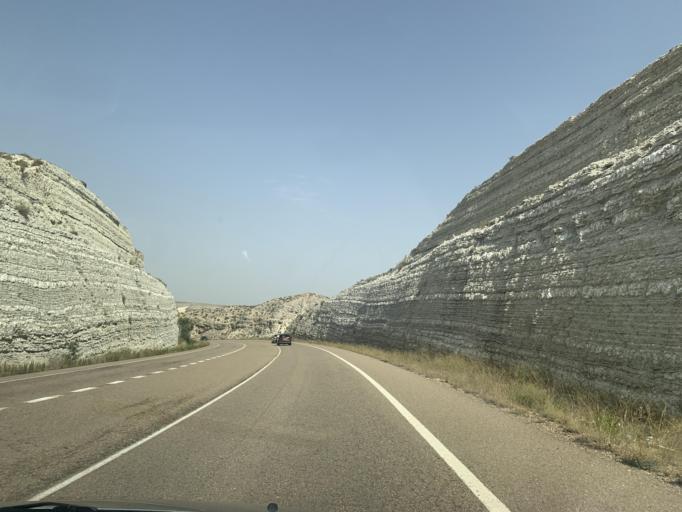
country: ES
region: Aragon
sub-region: Provincia de Zaragoza
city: Fuentes de Ebro
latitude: 41.4518
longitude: -0.7190
